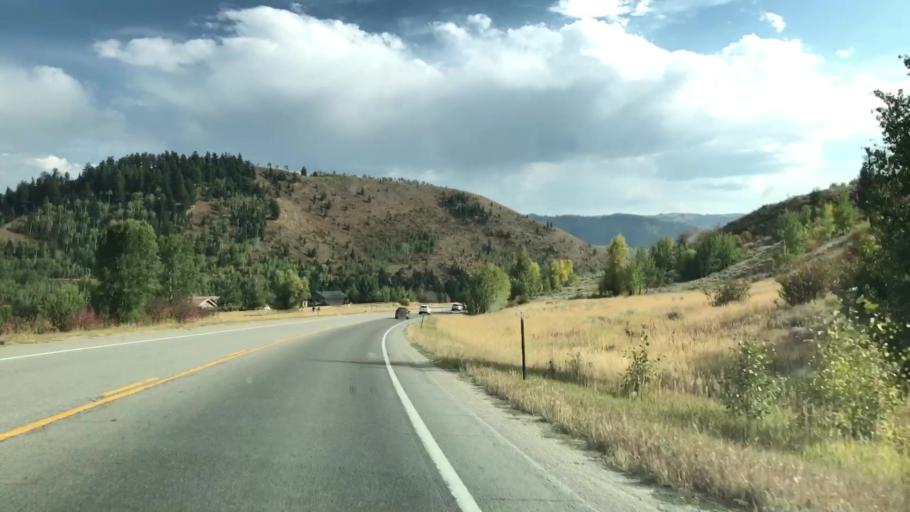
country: US
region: Wyoming
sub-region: Teton County
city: Hoback
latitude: 43.3549
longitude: -110.7207
